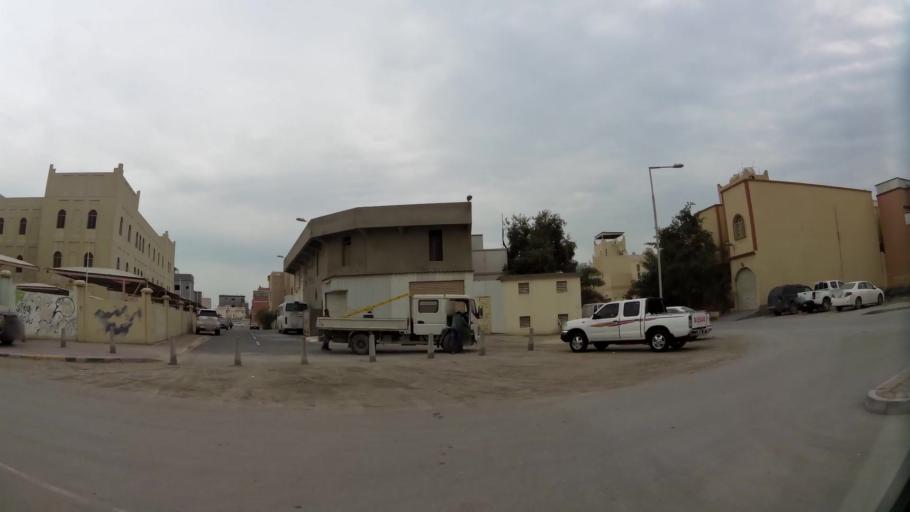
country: BH
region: Northern
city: Sitrah
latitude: 26.1388
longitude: 50.5995
